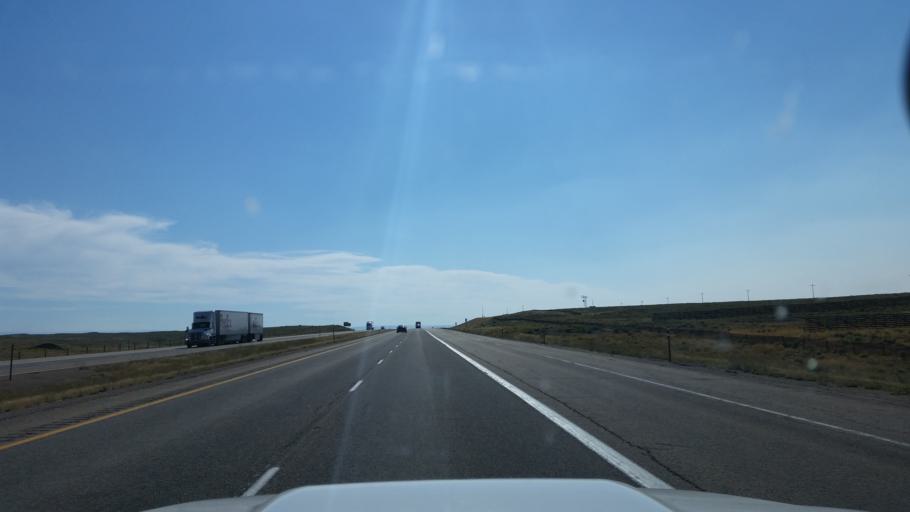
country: US
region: Wyoming
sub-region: Uinta County
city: Lyman
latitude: 41.4324
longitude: -110.1113
